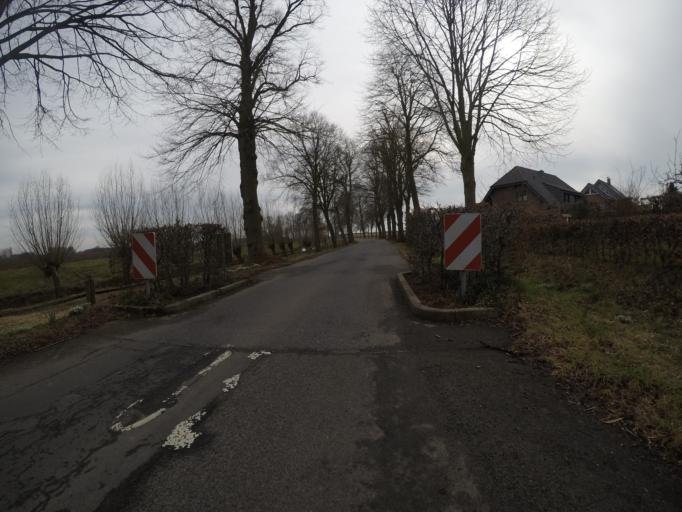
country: DE
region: North Rhine-Westphalia
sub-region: Regierungsbezirk Dusseldorf
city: Hamminkeln
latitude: 51.7716
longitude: 6.5690
